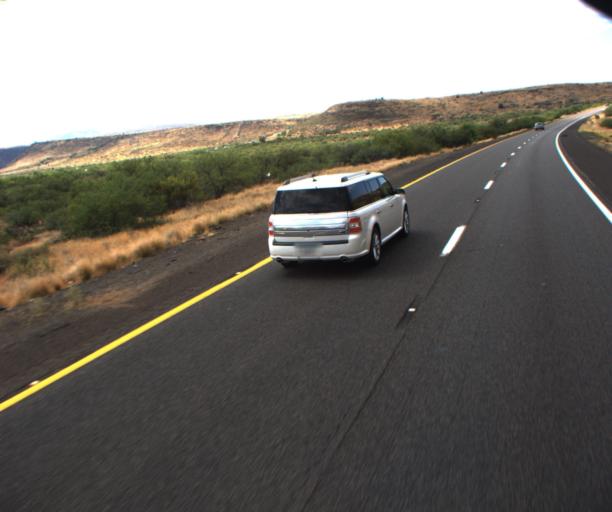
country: US
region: Arizona
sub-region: Yavapai County
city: Cordes Lakes
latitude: 34.2429
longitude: -112.1140
